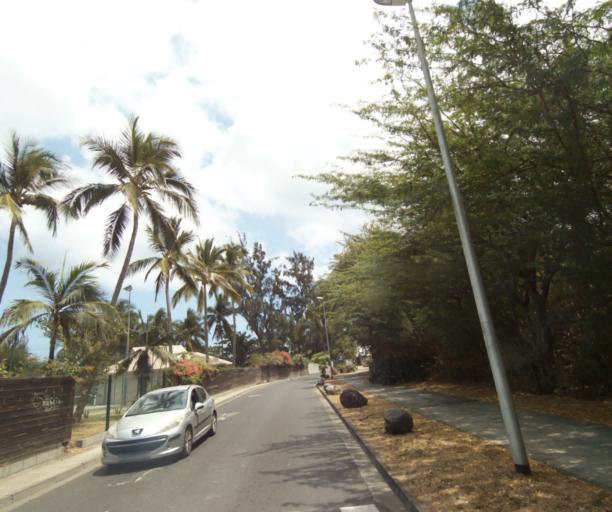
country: RE
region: Reunion
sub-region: Reunion
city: Saint-Paul
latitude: -21.0657
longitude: 55.2226
